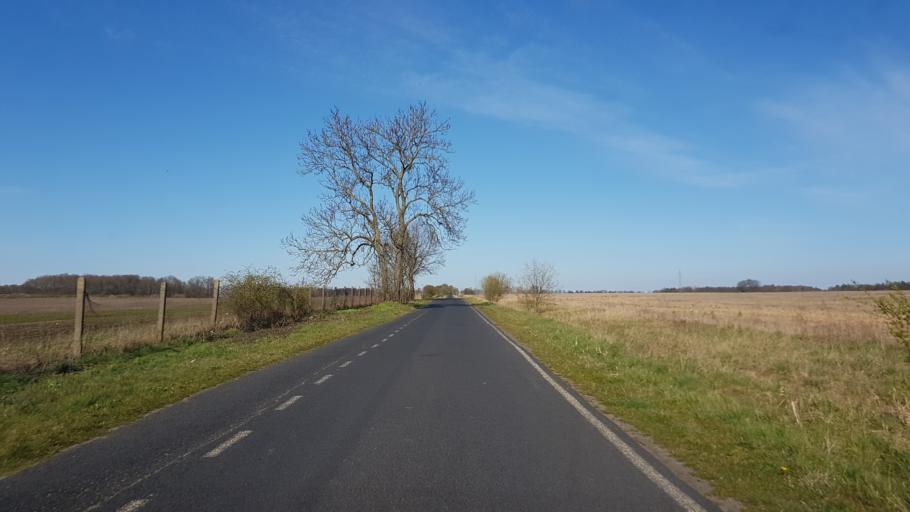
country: PL
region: West Pomeranian Voivodeship
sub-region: Powiat stargardzki
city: Stargard Szczecinski
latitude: 53.4069
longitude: 15.0354
